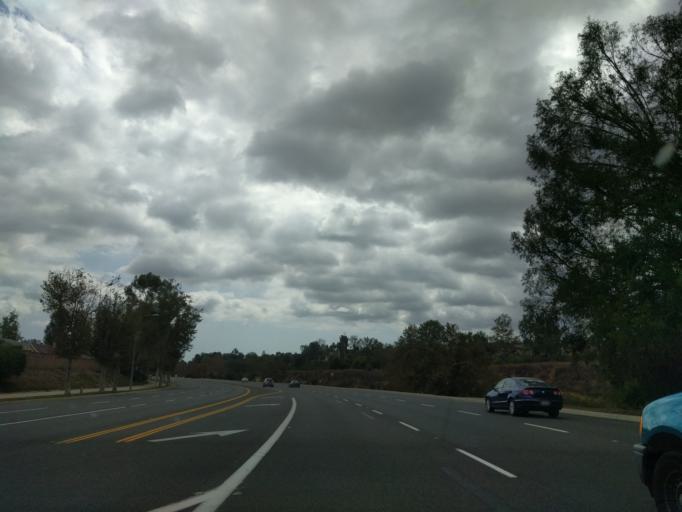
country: US
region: California
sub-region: Orange County
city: Foothill Ranch
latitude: 33.6583
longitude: -117.6567
